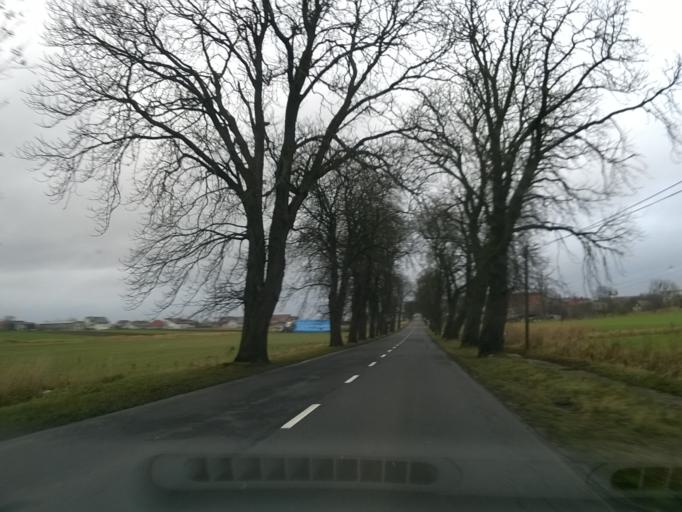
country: PL
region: Kujawsko-Pomorskie
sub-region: Powiat nakielski
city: Kcynia
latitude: 52.9871
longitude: 17.4728
